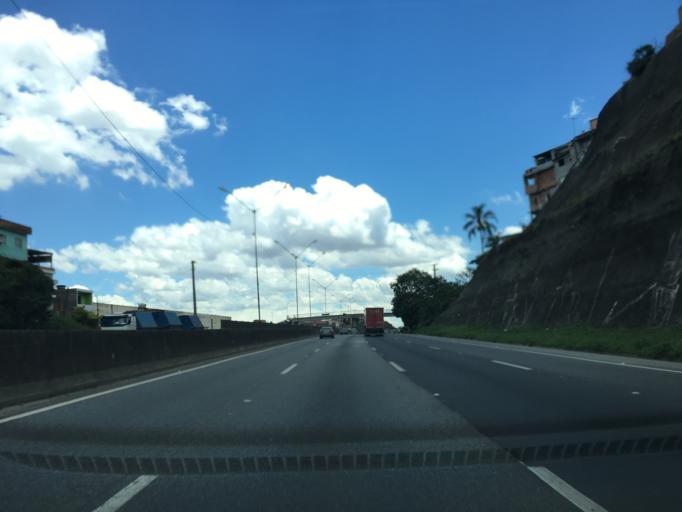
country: BR
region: Sao Paulo
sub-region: Guarulhos
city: Guarulhos
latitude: -23.4347
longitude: -46.5686
